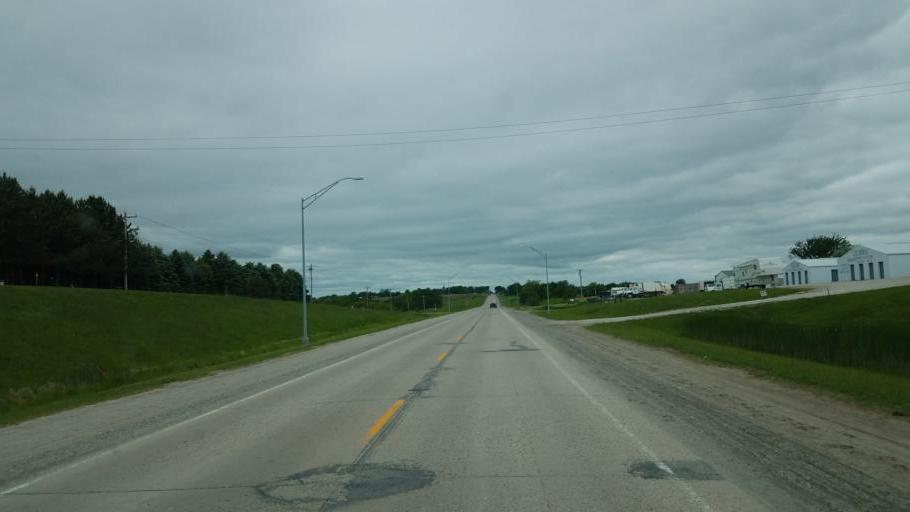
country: US
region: Iowa
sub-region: Decatur County
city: Lamoni
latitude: 40.6236
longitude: -93.9029
